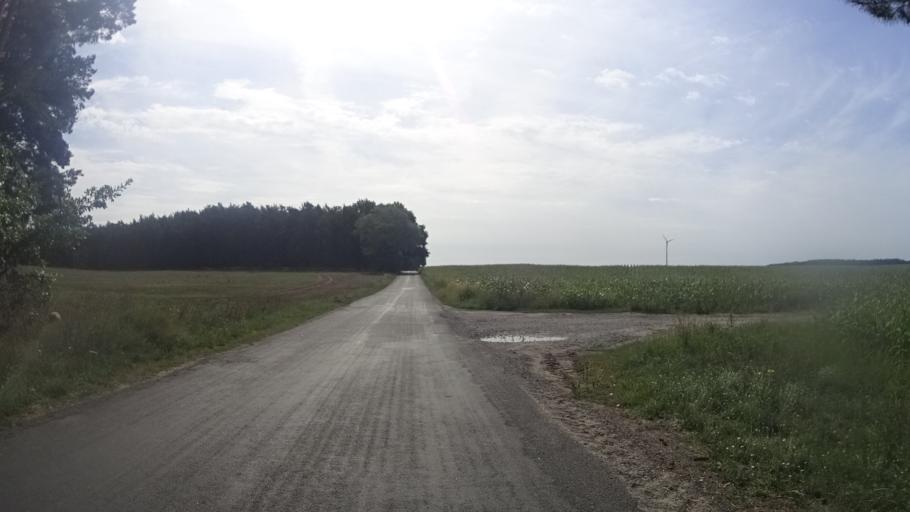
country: DE
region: Brandenburg
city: Golzow
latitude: 52.3203
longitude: 12.6812
